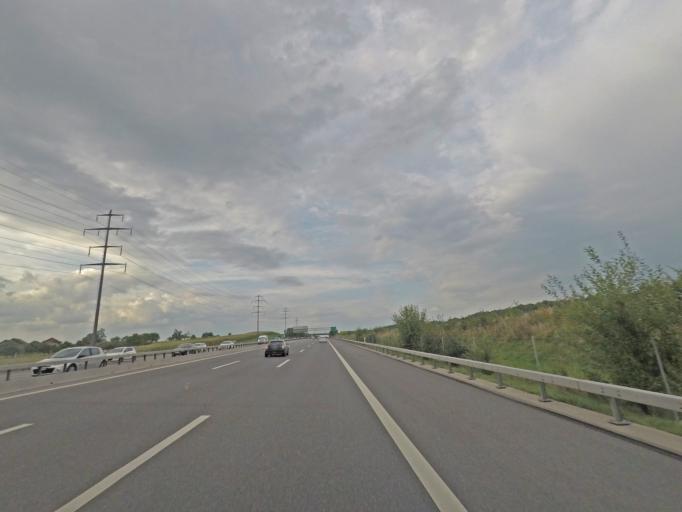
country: CH
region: Zug
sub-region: Zug
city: Hunenberg
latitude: 47.1655
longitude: 8.4329
